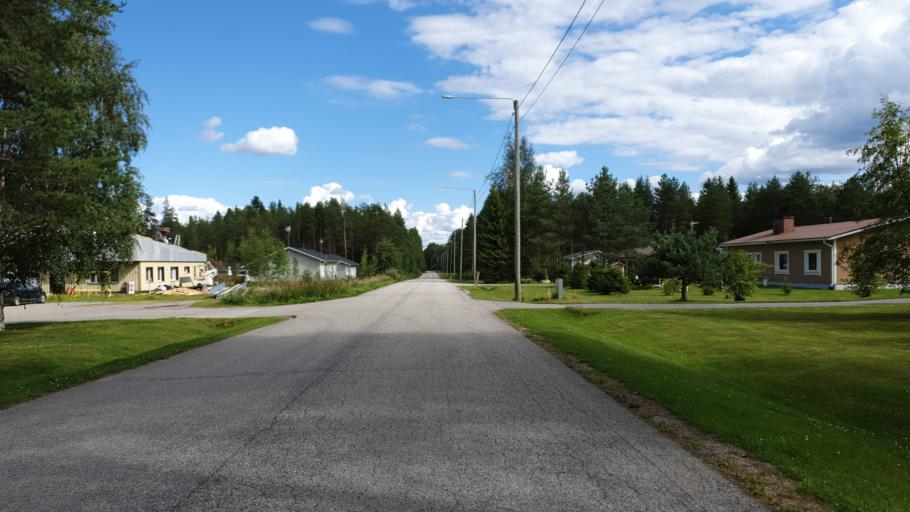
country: FI
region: Kainuu
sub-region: Kehys-Kainuu
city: Kuhmo
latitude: 64.1196
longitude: 29.5552
